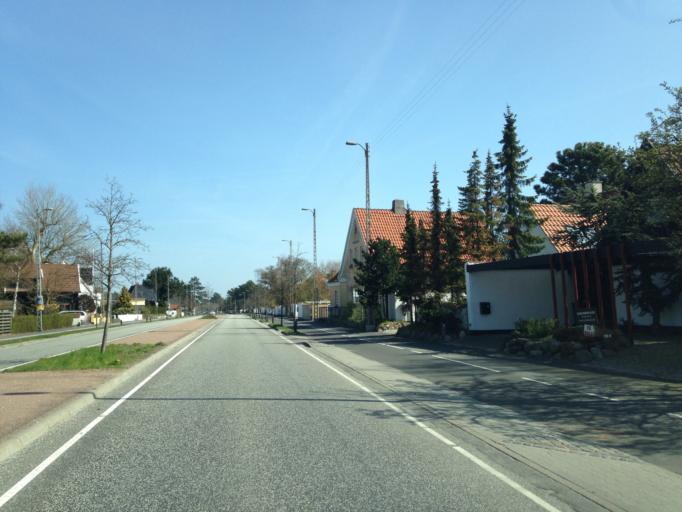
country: DK
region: Zealand
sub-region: Greve Kommune
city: Greve
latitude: 55.5732
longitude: 12.2910
